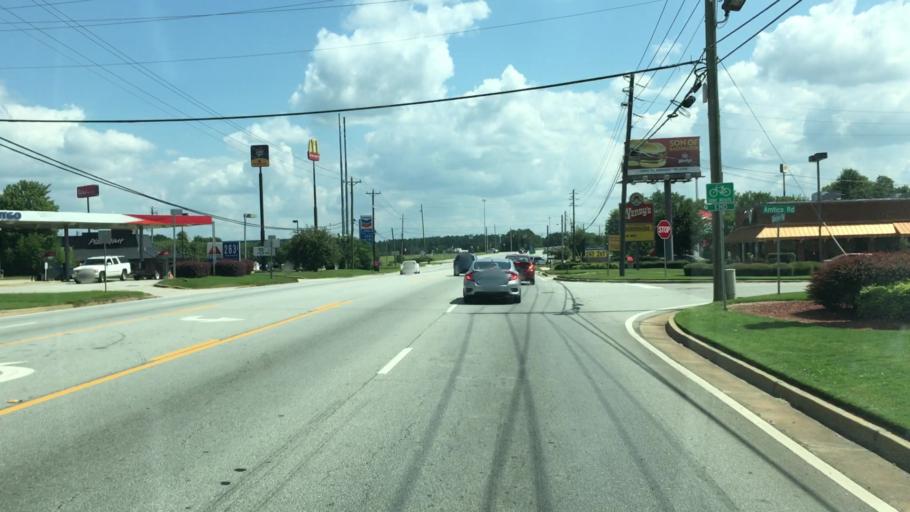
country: US
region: Georgia
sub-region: Morgan County
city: Madison
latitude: 33.5594
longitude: -83.4768
